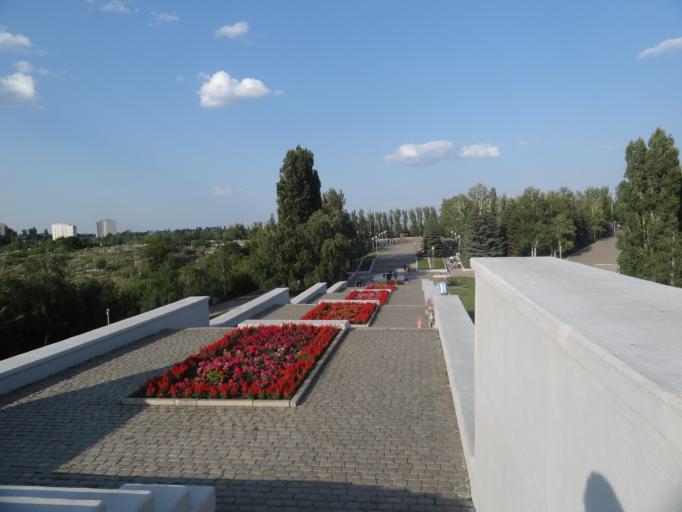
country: RU
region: Saratov
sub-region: Saratovskiy Rayon
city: Saratov
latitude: 51.5444
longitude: 46.0498
